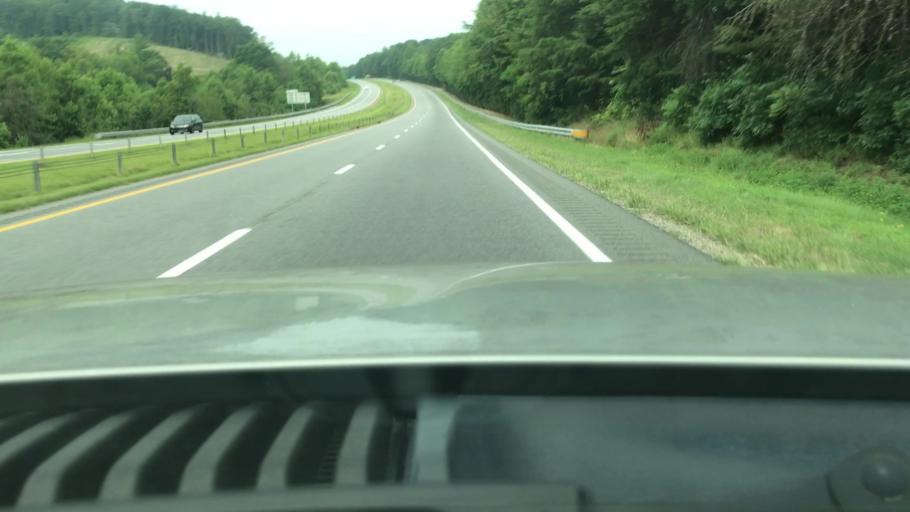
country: US
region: North Carolina
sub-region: Wilkes County
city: North Wilkesboro
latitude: 36.1455
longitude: -81.0534
